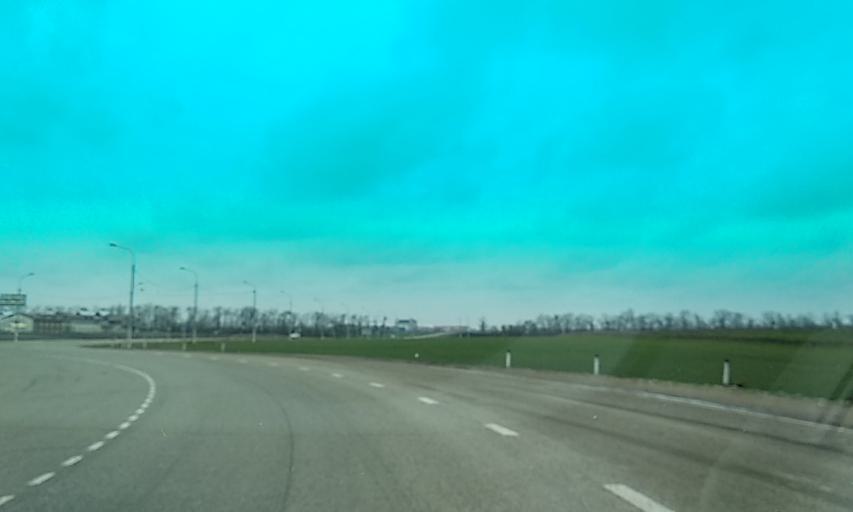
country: RU
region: Krasnodarskiy
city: Vyselki
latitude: 45.5861
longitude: 39.7049
